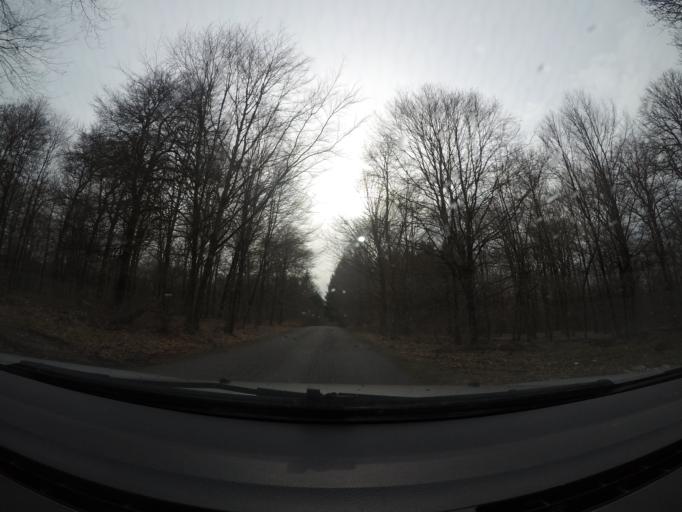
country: BE
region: Wallonia
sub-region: Province du Luxembourg
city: Martelange
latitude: 49.8210
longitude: 5.7114
